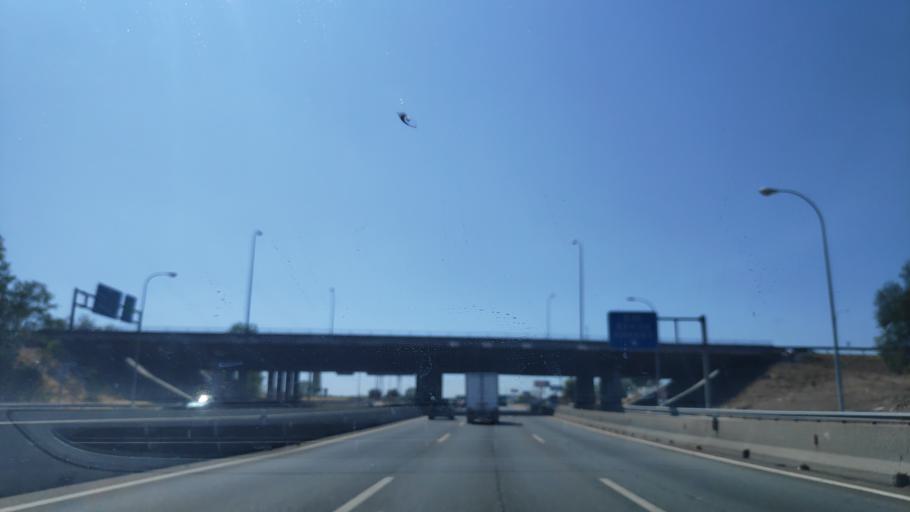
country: ES
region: Madrid
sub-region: Provincia de Madrid
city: Carabanchel
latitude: 40.3656
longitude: -3.7207
